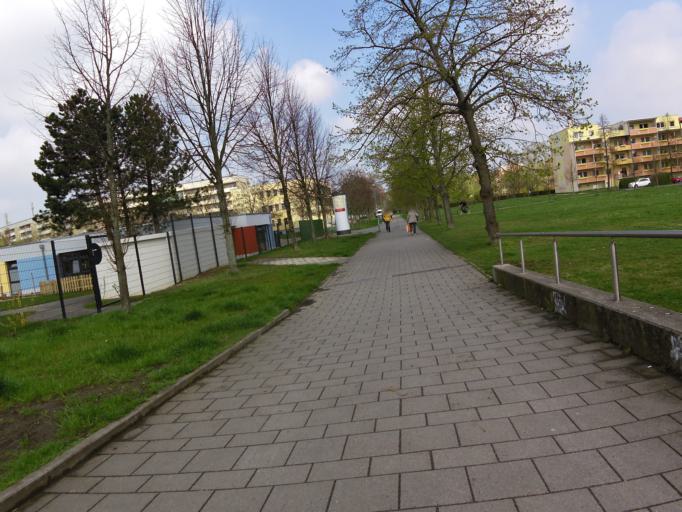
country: DE
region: Saxony
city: Markranstadt
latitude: 51.3224
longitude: 12.2693
